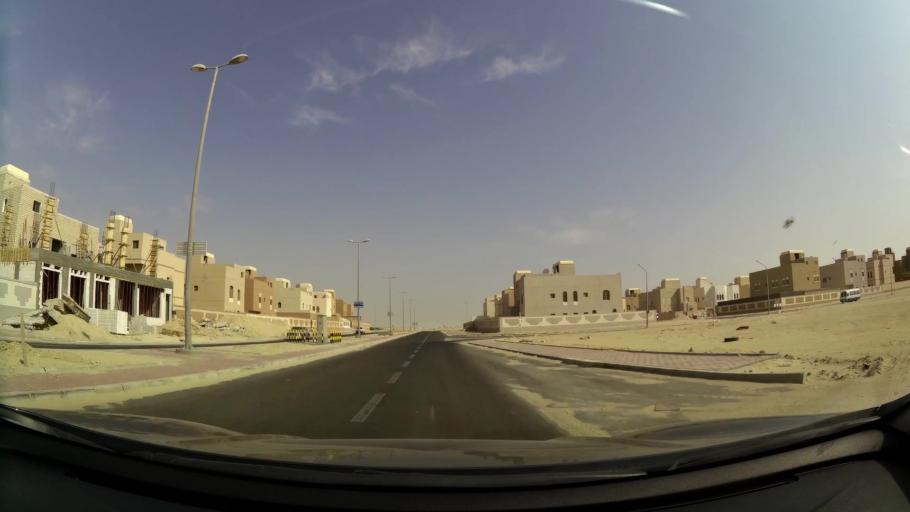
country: KW
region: Al Ahmadi
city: Al Wafrah
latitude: 28.8008
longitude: 48.0746
